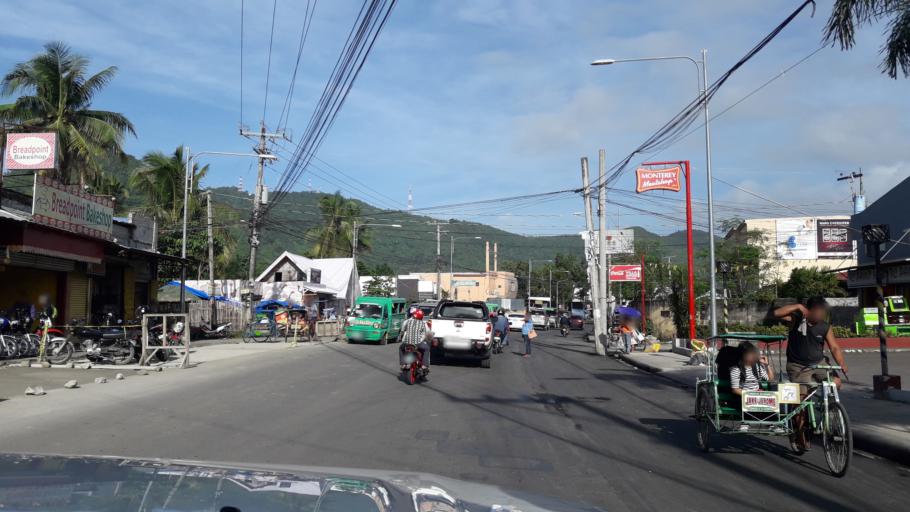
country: PH
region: Eastern Visayas
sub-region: Province of Leyte
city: Panalanoy
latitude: 11.2165
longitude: 124.9955
